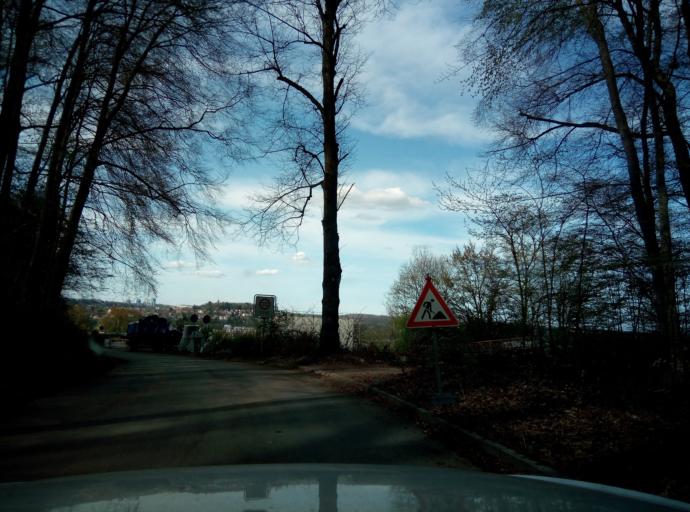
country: DE
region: Baden-Wuerttemberg
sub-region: Tuebingen Region
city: Tuebingen
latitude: 48.5046
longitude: 9.0727
